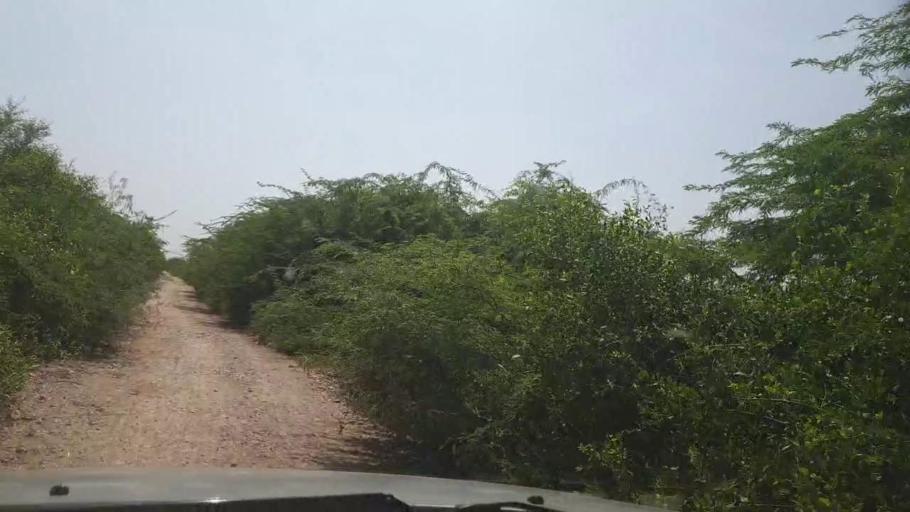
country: PK
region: Sindh
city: Tando Ghulam Ali
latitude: 25.1153
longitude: 68.8101
